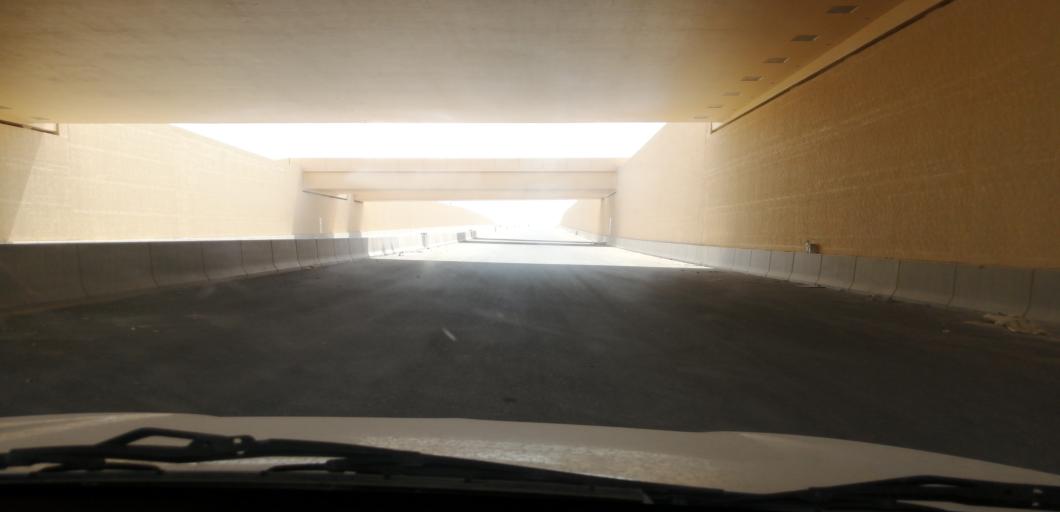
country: KW
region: Muhafazat al Jahra'
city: Al Jahra'
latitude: 29.4506
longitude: 47.6056
